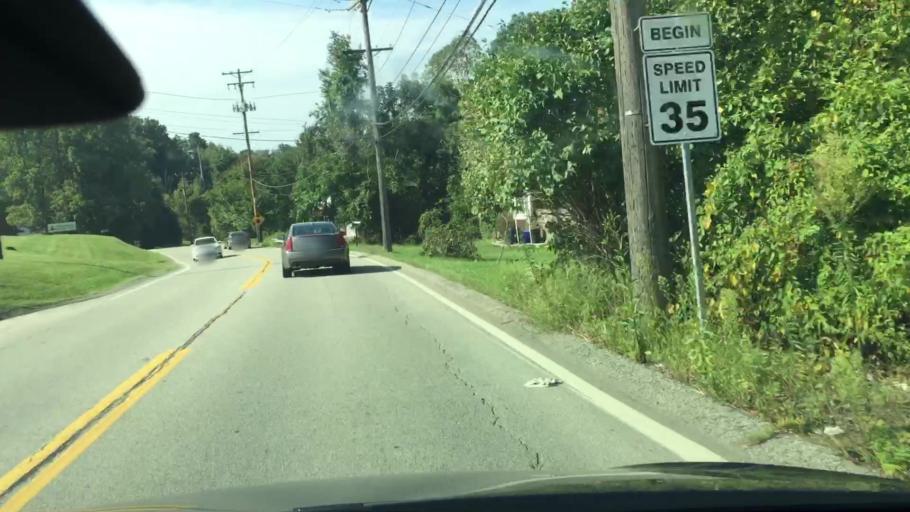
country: US
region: Pennsylvania
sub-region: Allegheny County
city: Monroeville
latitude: 40.4325
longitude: -79.7607
